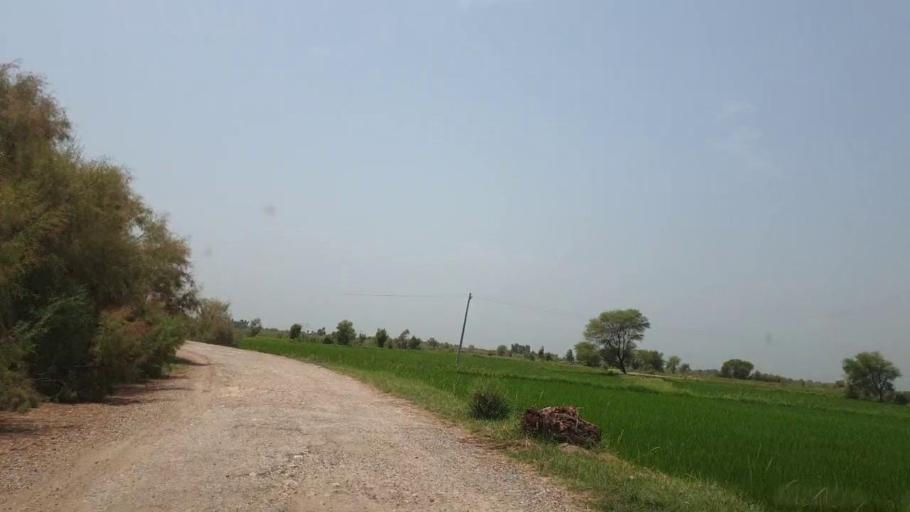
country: PK
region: Sindh
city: Shikarpur
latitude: 27.8969
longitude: 68.6319
